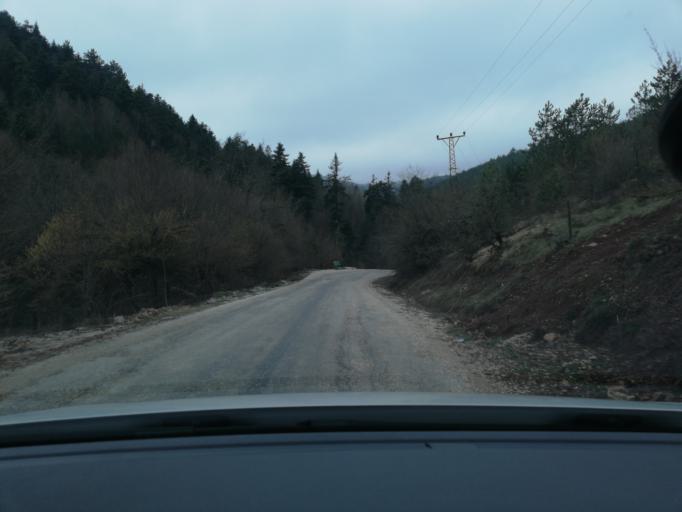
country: TR
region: Bolu
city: Bolu
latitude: 40.6842
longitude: 31.4578
